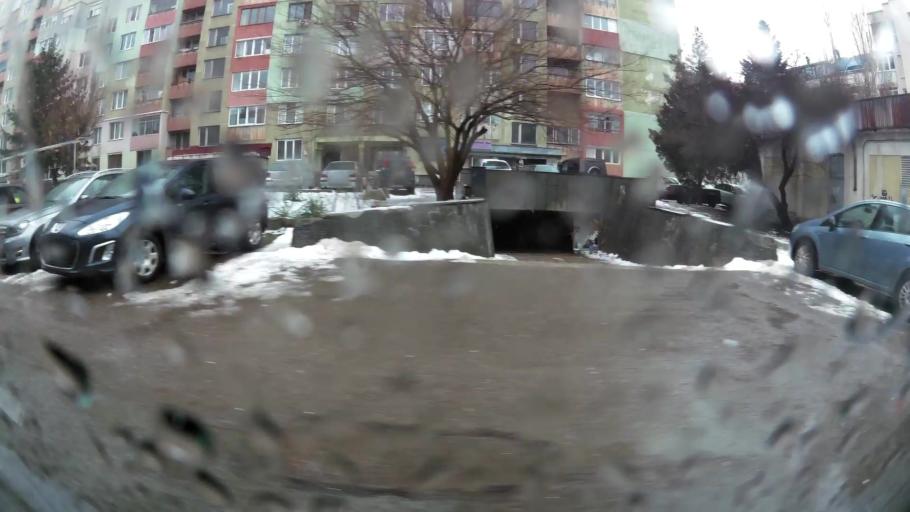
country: BG
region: Sofia-Capital
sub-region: Stolichna Obshtina
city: Sofia
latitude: 42.6649
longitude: 23.2996
